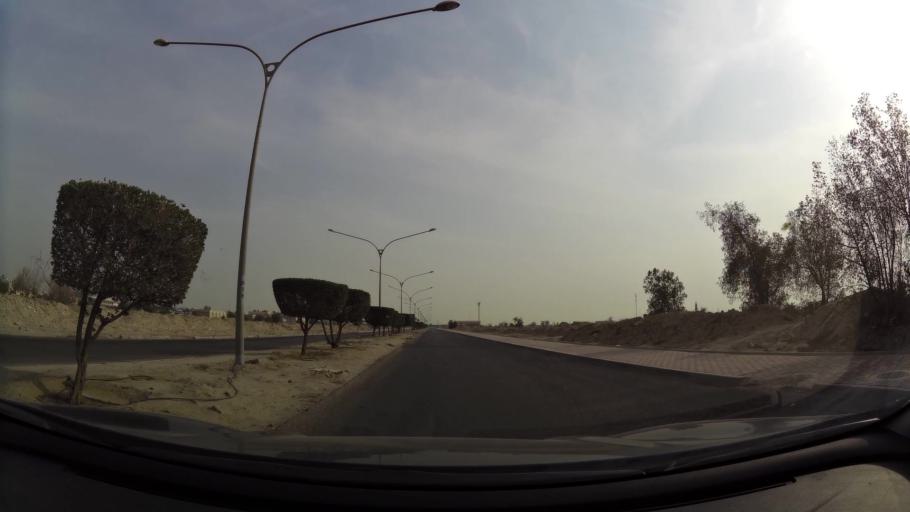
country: KW
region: Al Farwaniyah
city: Janub as Surrah
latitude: 29.2740
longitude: 47.9789
